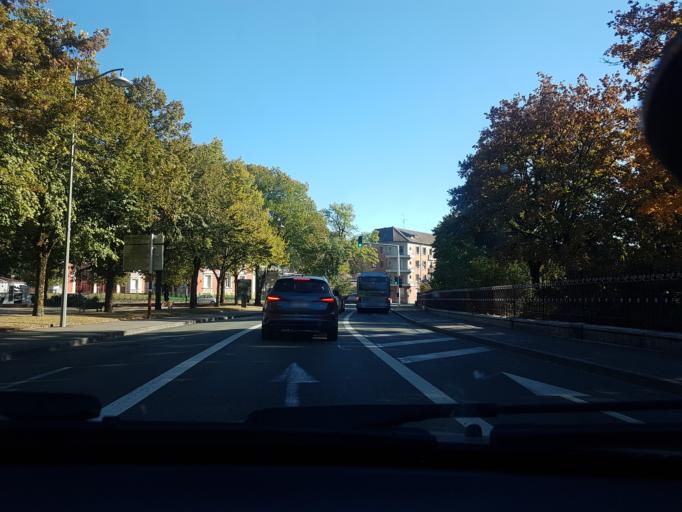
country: FR
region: Franche-Comte
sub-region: Territoire de Belfort
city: Belfort
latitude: 47.6361
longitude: 6.8609
